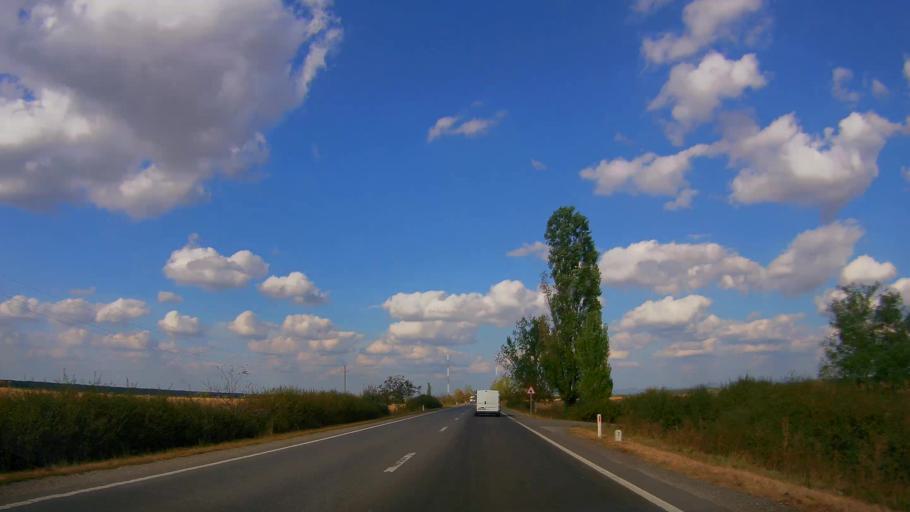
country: RO
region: Satu Mare
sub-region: Comuna Botiz
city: Botiz
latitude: 47.8430
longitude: 22.9639
